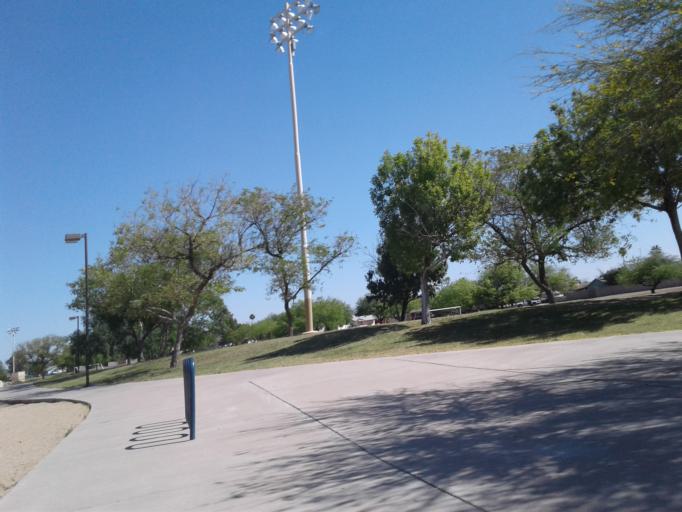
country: US
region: Arizona
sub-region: Maricopa County
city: Paradise Valley
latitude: 33.6162
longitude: -112.0118
